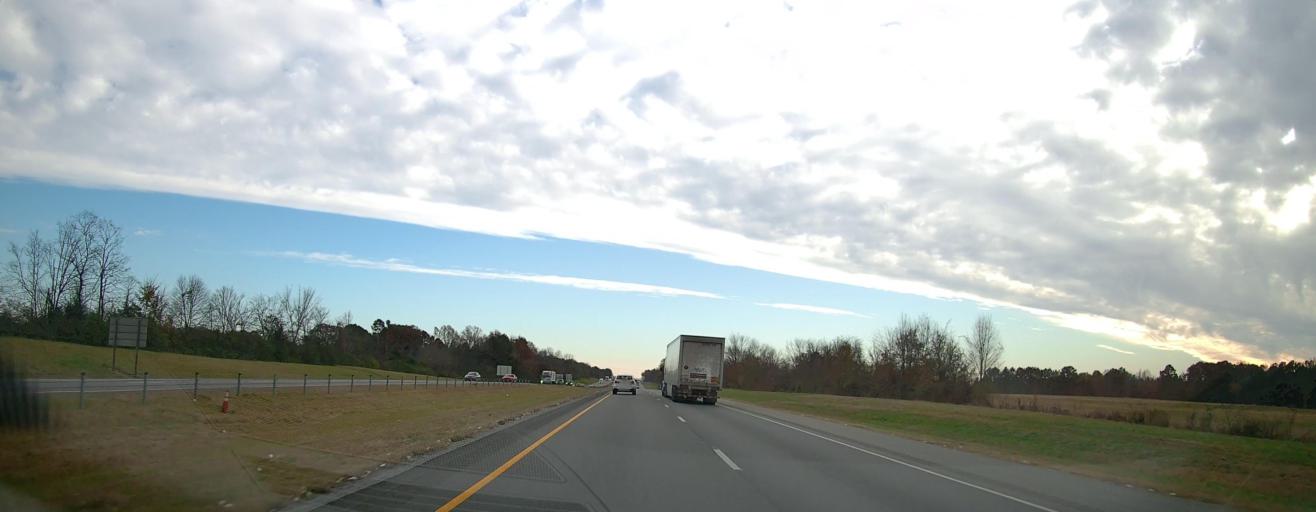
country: US
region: Alabama
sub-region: Limestone County
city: Athens
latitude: 34.7707
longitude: -86.9398
